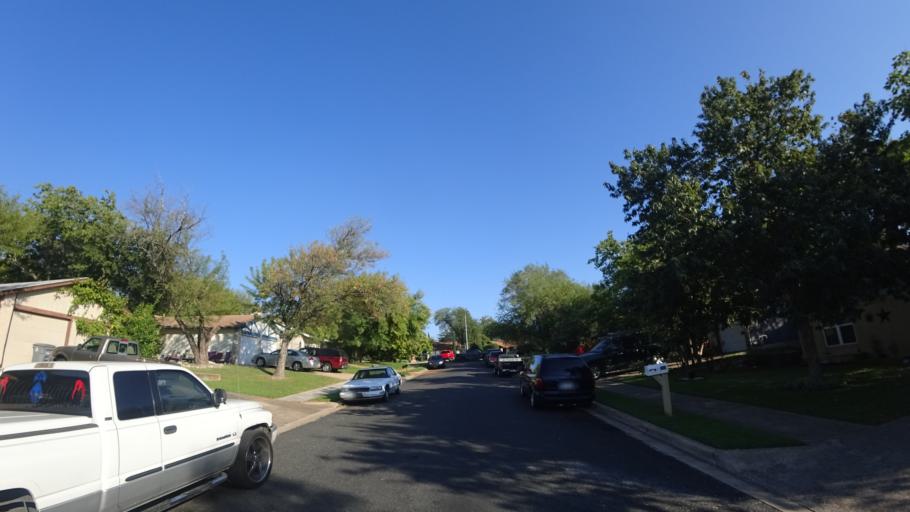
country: US
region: Texas
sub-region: Travis County
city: Wells Branch
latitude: 30.3569
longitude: -97.6815
